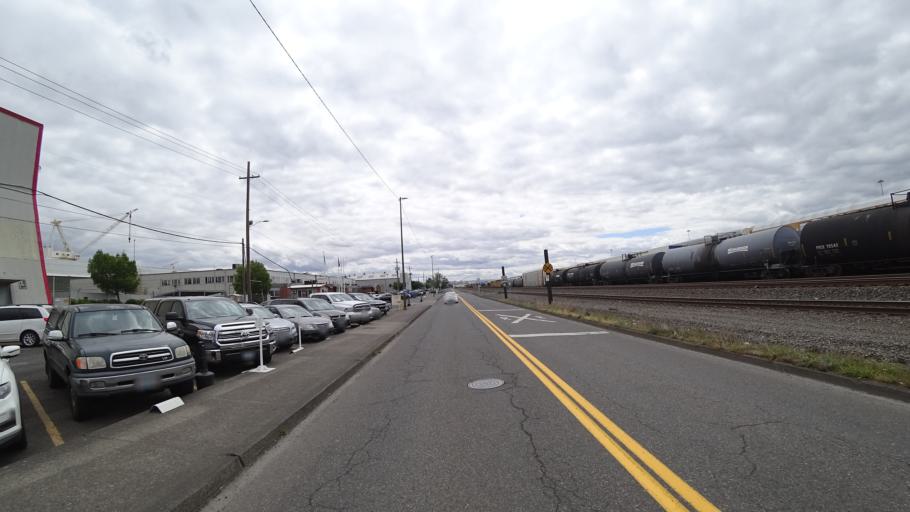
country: US
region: Oregon
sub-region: Multnomah County
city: Portland
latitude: 45.5540
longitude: -122.7206
